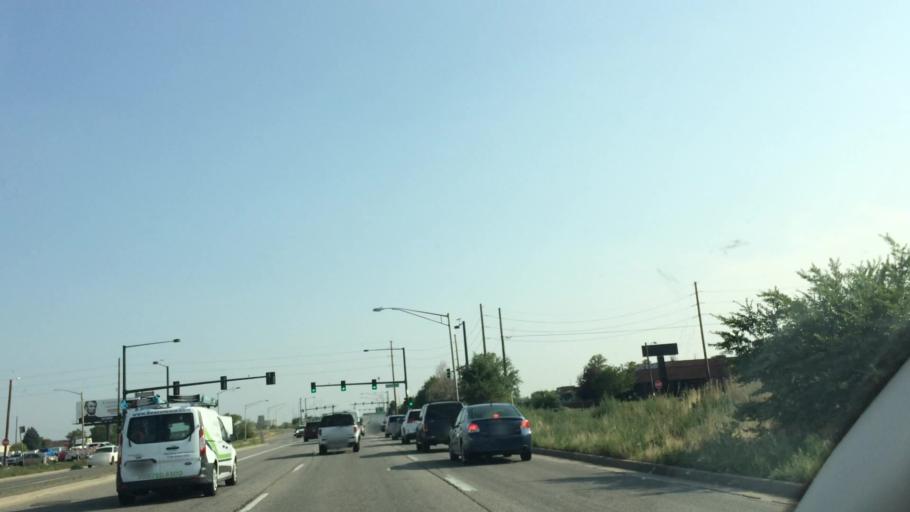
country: US
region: Colorado
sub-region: Adams County
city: Commerce City
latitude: 39.7847
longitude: -104.9406
